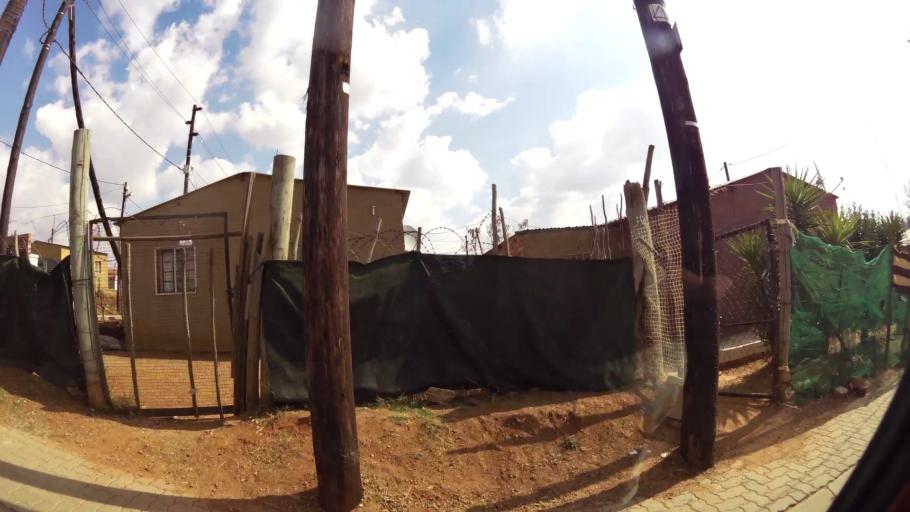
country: ZA
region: Gauteng
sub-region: City of Johannesburg Metropolitan Municipality
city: Roodepoort
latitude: -26.1831
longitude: 27.8458
